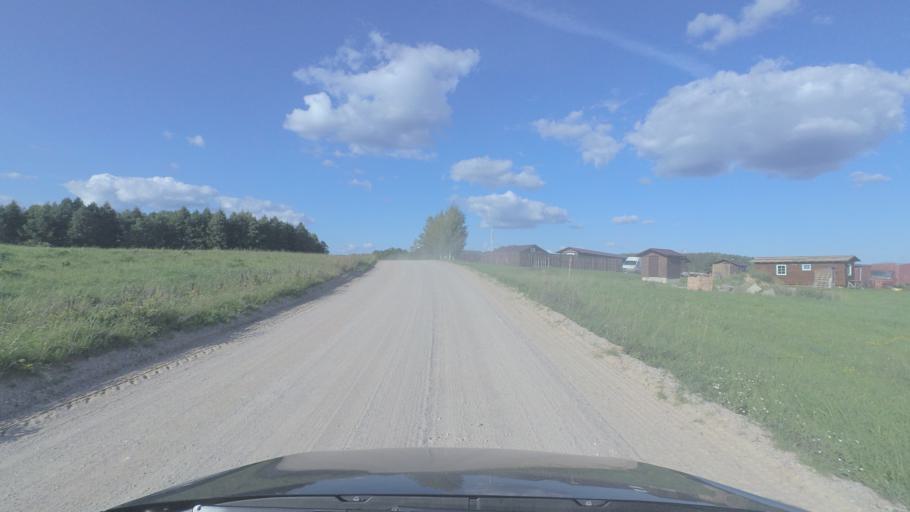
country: LT
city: Pabrade
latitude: 55.1361
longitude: 25.7091
